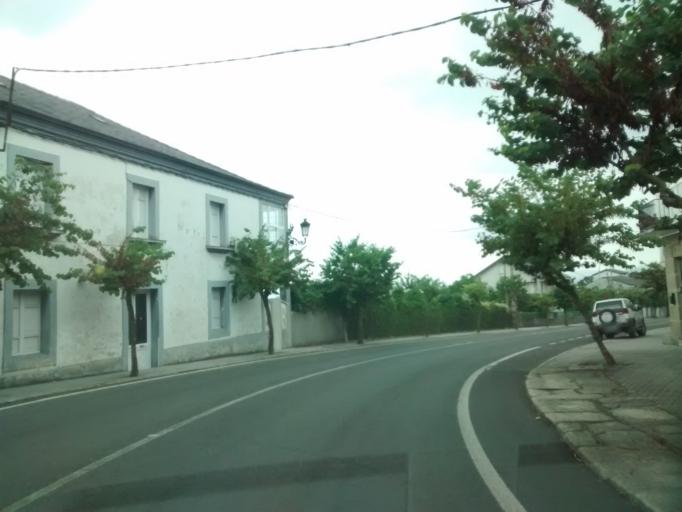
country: ES
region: Galicia
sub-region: Provincia de Ourense
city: Manzaneda
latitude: 42.3415
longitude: -7.2501
